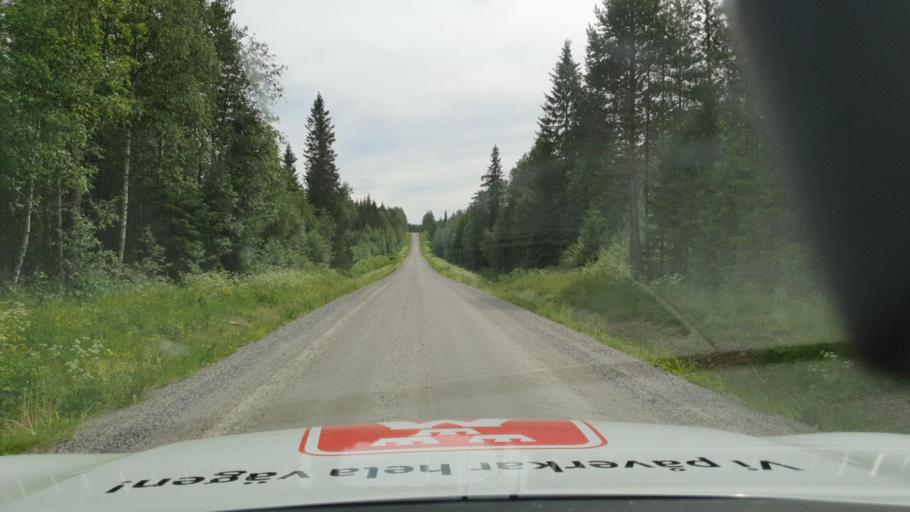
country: SE
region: Vaesterbotten
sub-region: Skelleftea Kommun
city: Burea
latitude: 64.4492
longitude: 21.0244
